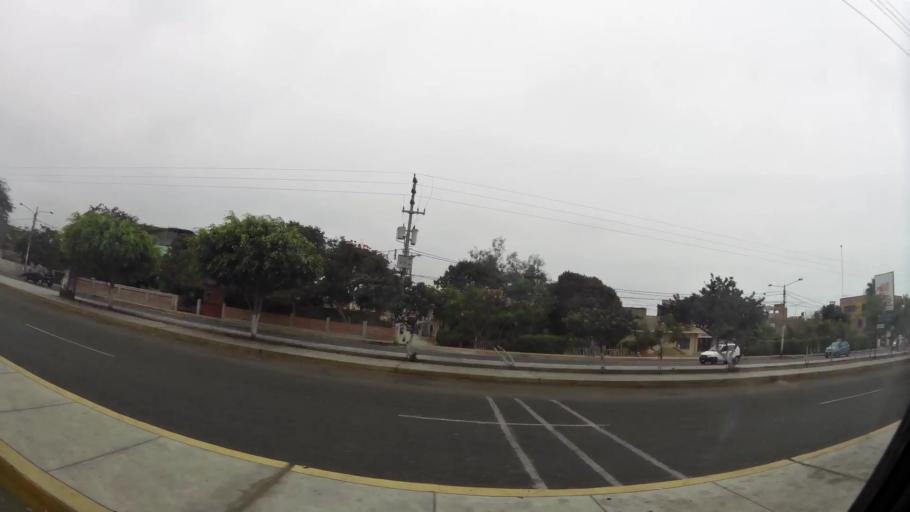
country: PE
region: Ancash
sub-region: Provincia de Santa
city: Chimbote
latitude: -9.0657
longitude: -78.5830
